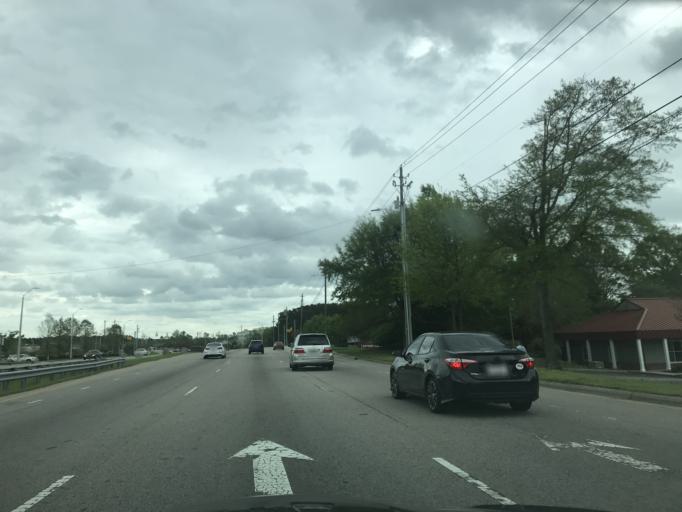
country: US
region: North Carolina
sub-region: Wake County
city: Knightdale
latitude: 35.7956
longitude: -78.5124
